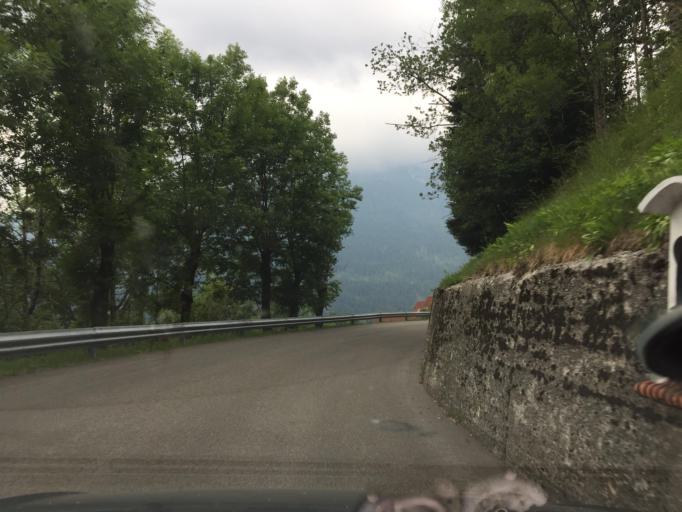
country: IT
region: Friuli Venezia Giulia
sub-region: Provincia di Udine
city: Rigolato
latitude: 46.5790
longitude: 12.8149
